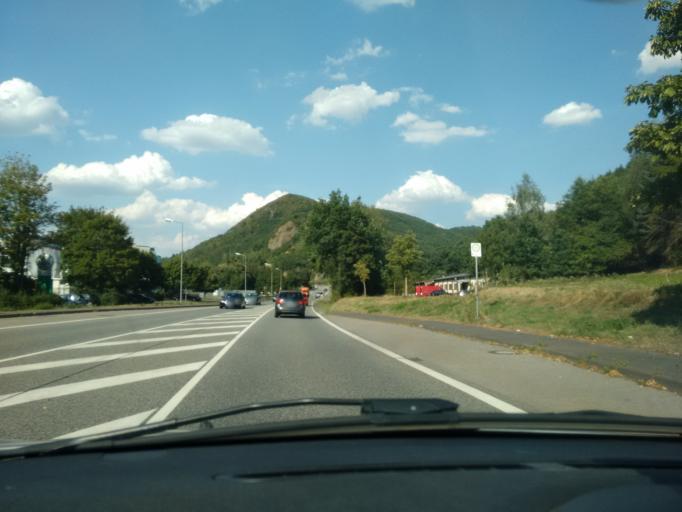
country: DE
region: Rheinland-Pfalz
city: Kirn
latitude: 49.7710
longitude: 7.4488
